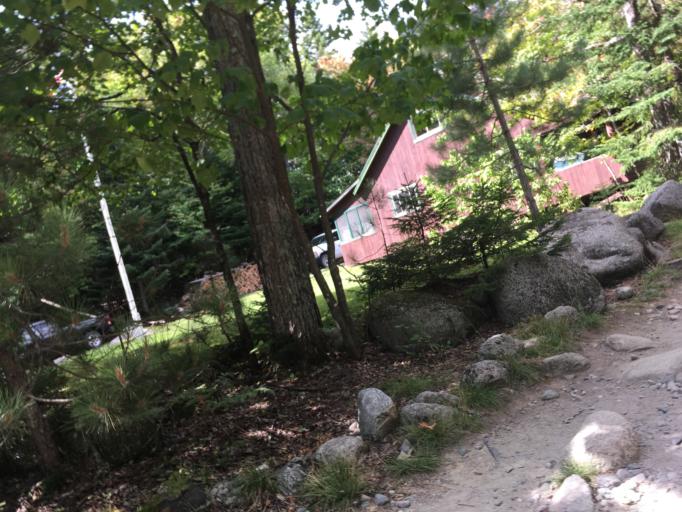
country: US
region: Maine
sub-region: Penobscot County
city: Millinocket
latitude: 45.9197
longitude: -68.8574
